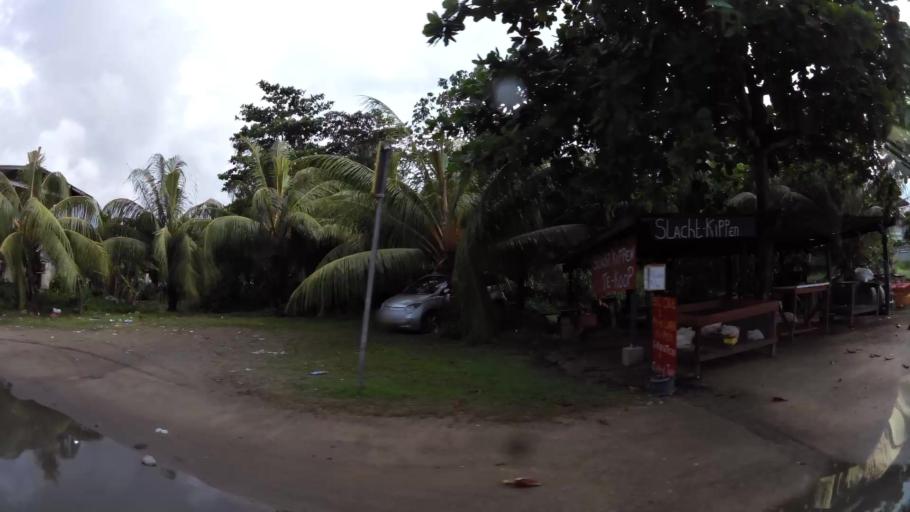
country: SR
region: Paramaribo
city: Paramaribo
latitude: 5.8424
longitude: -55.2068
